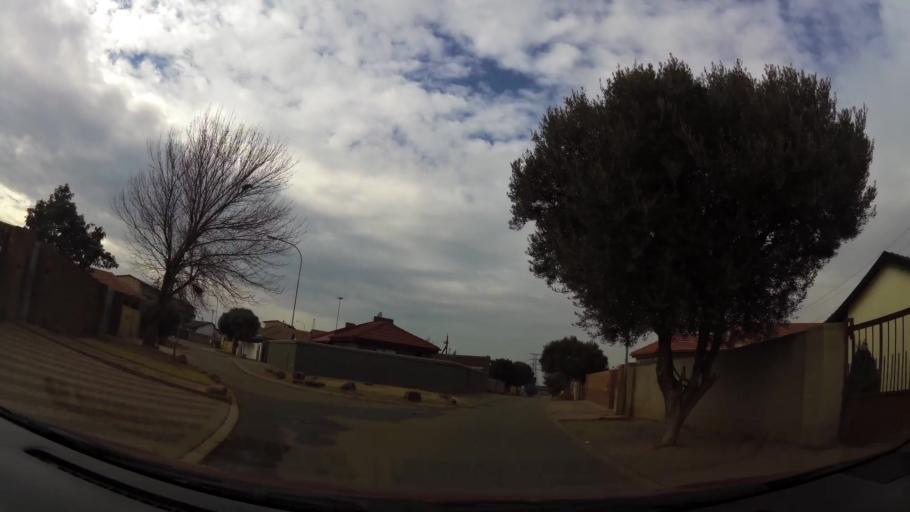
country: ZA
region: Gauteng
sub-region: City of Johannesburg Metropolitan Municipality
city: Soweto
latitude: -26.2730
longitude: 27.8406
